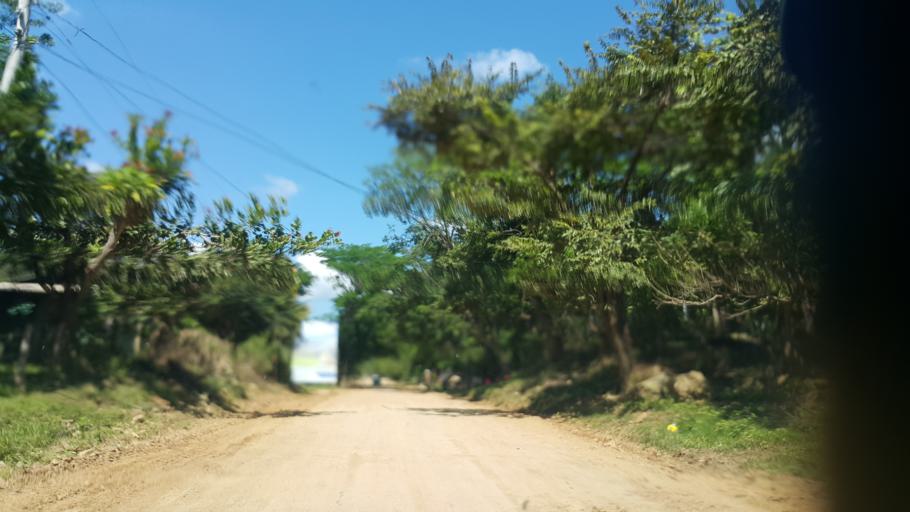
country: NI
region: Rivas
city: San Juan del Sur
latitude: 11.2853
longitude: -85.8896
